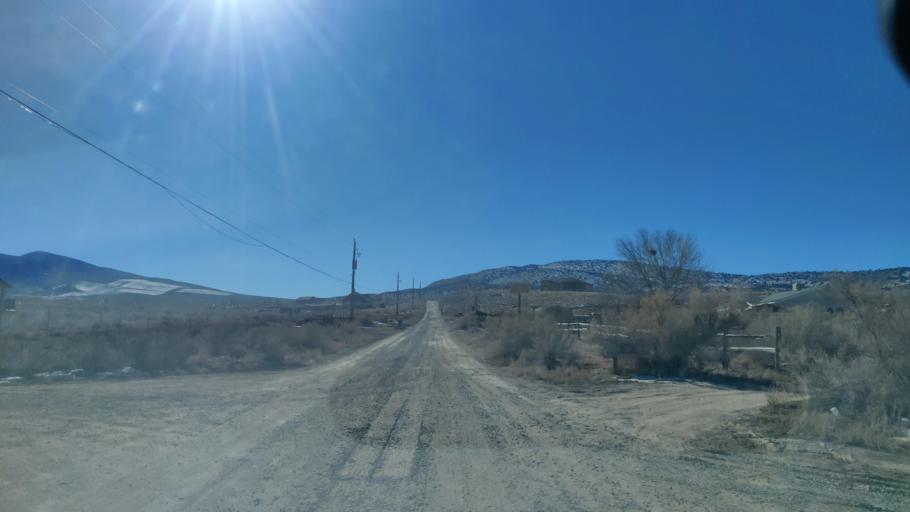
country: US
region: Colorado
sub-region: Mesa County
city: Palisade
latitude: 39.0916
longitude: -108.3296
